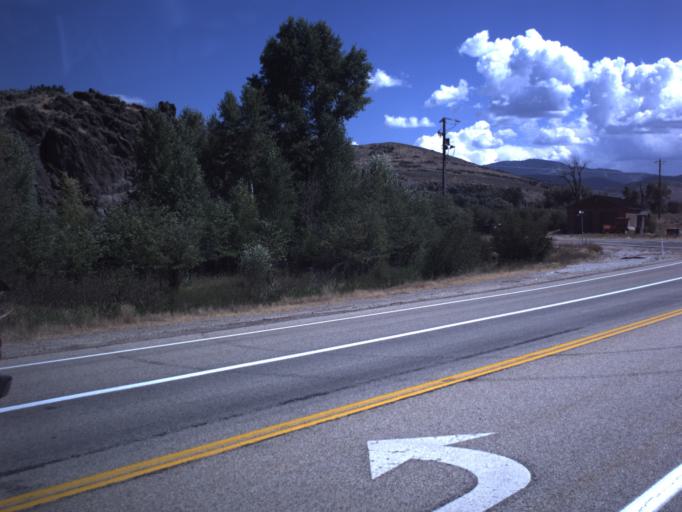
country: US
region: Utah
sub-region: Summit County
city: Francis
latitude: 40.6015
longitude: -111.3298
